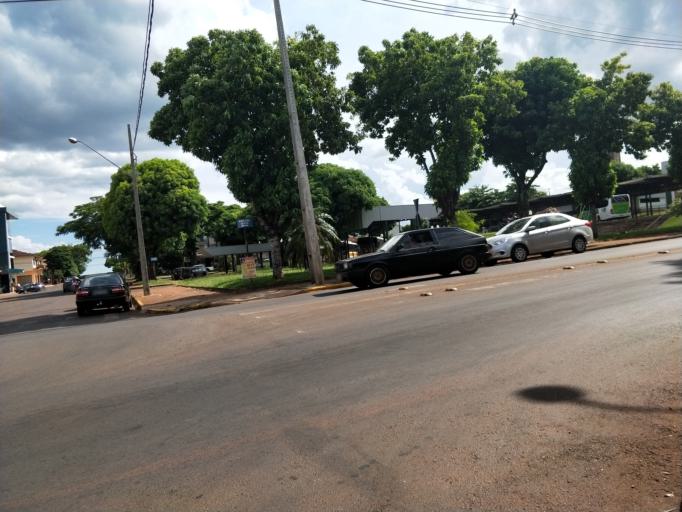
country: BR
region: Parana
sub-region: Marechal Candido Rondon
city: Marechal Candido Rondon
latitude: -24.5658
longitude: -54.0573
